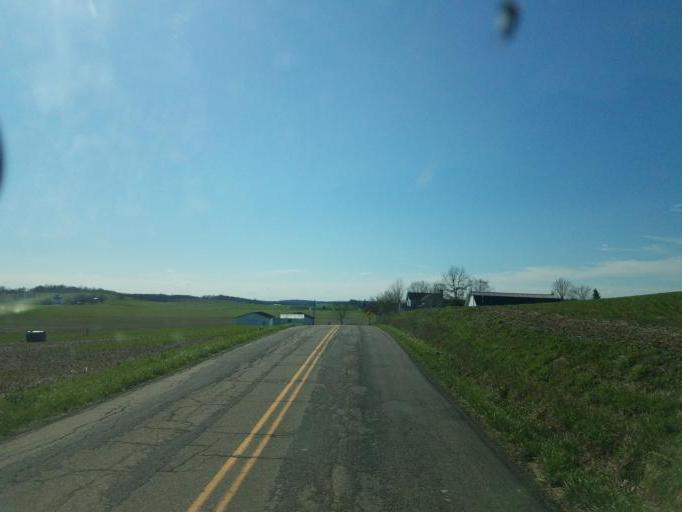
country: US
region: Ohio
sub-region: Knox County
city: Danville
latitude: 40.4355
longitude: -82.2506
